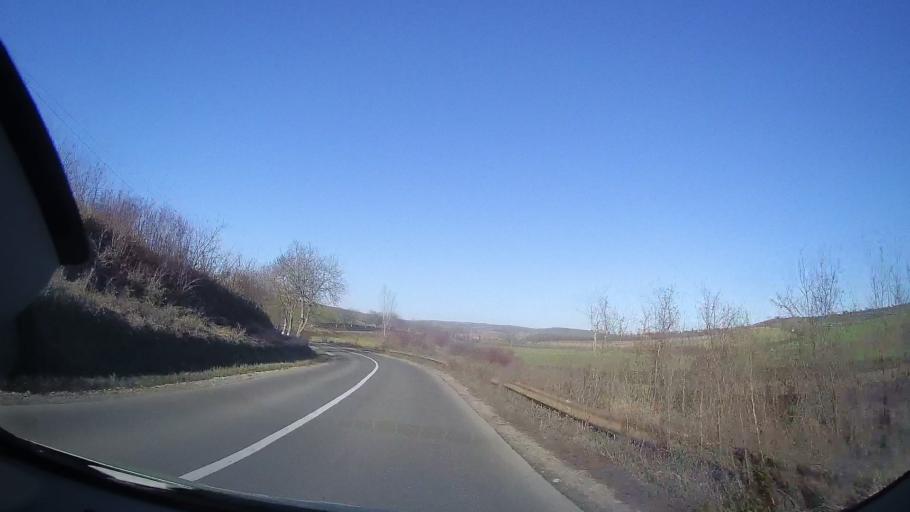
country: RO
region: Mures
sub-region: Comuna Sarmasu
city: Balda
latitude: 46.7370
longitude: 24.1495
